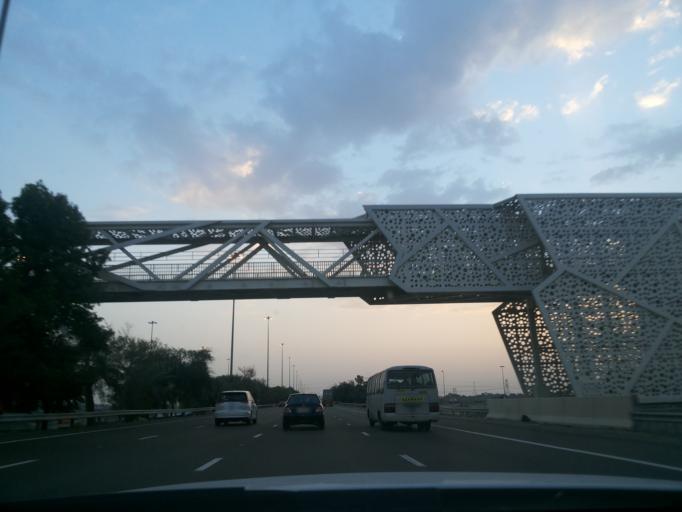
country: AE
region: Abu Dhabi
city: Abu Dhabi
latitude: 24.6702
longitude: 54.7605
